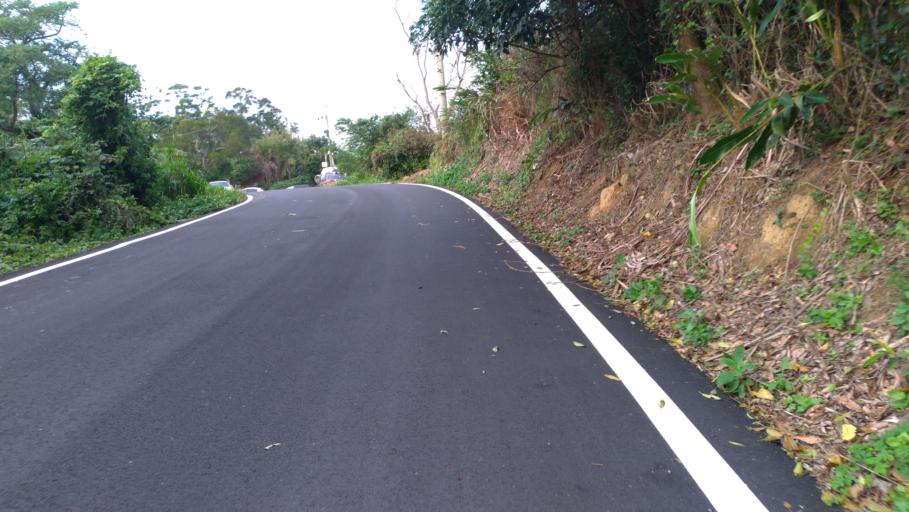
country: TW
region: Taiwan
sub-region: Hsinchu
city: Hsinchu
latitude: 24.7529
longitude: 120.9907
